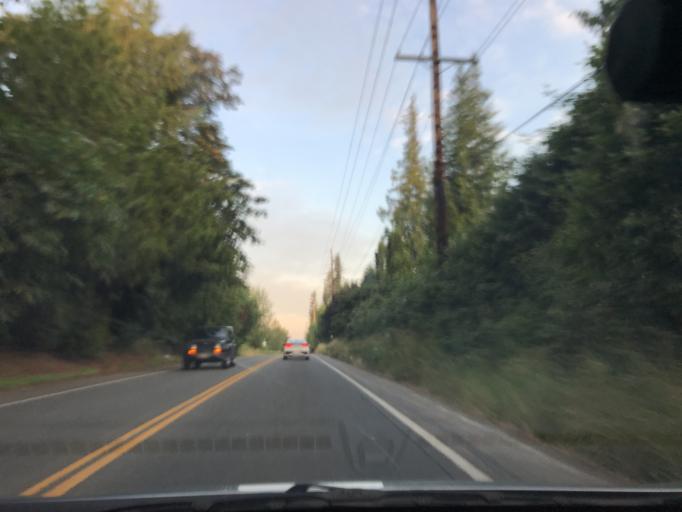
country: US
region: Washington
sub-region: King County
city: Maple Valley
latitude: 47.3581
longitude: -122.0469
